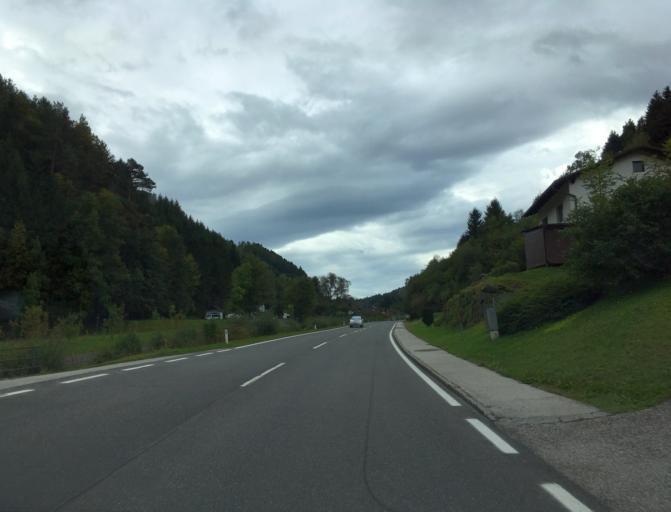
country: AT
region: Lower Austria
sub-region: Politischer Bezirk Neunkirchen
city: Thomasberg
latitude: 47.5744
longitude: 16.1430
